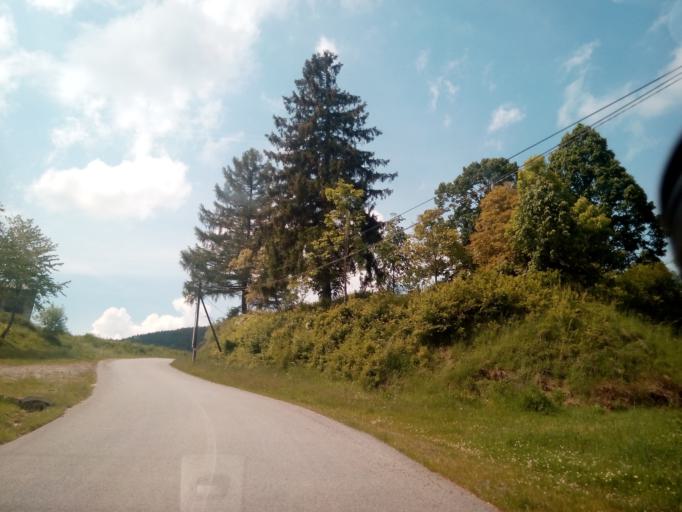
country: SK
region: Presovsky
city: Lipany
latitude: 49.0611
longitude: 20.9514
